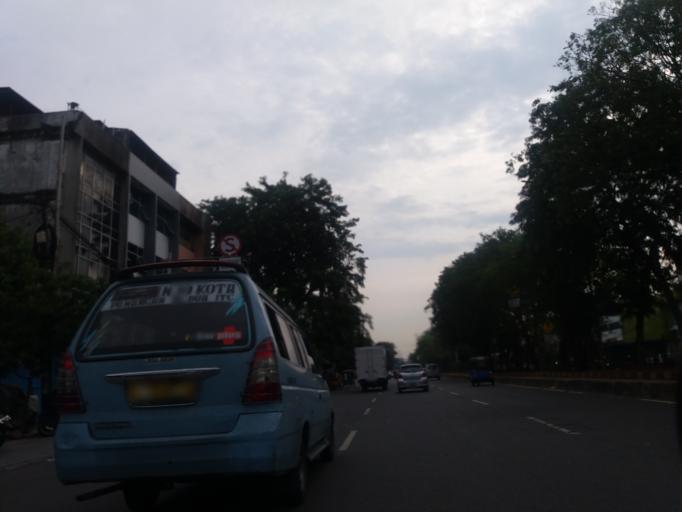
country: ID
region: Jakarta Raya
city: Jakarta
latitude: -6.1372
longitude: 106.8206
